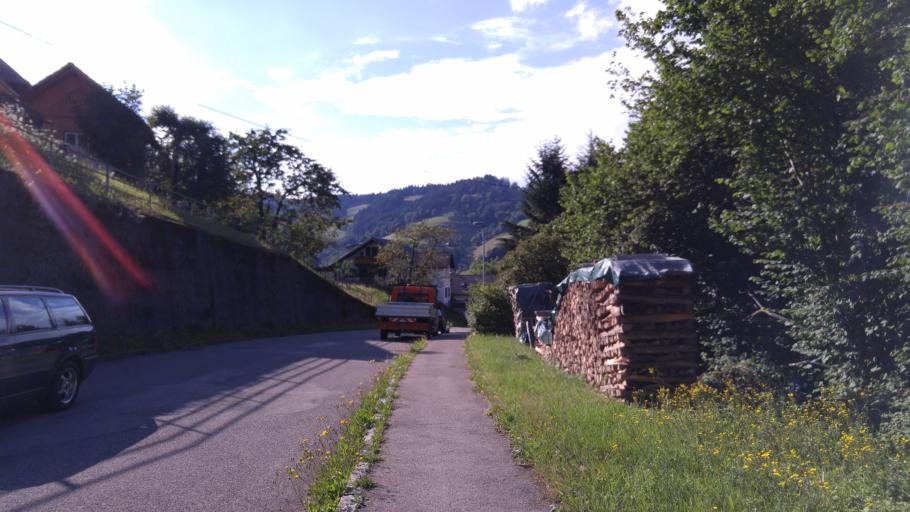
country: DE
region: Baden-Wuerttemberg
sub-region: Freiburg Region
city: Wieden
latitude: 47.8725
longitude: 7.8442
